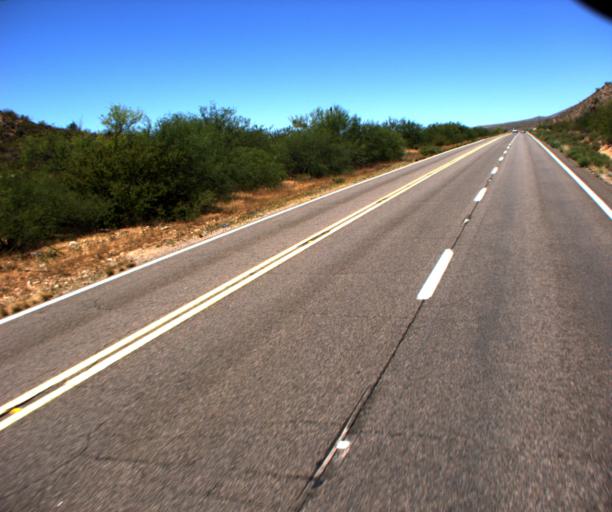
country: US
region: Arizona
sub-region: Pinal County
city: Kearny
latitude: 33.1311
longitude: -110.7810
